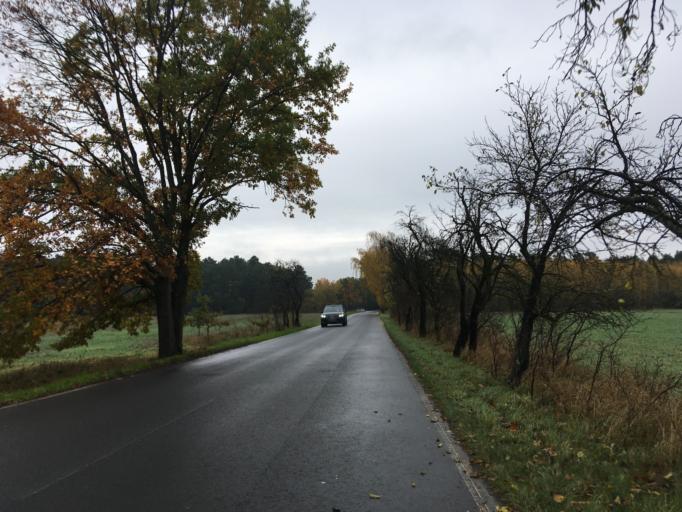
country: DE
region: Brandenburg
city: Friedland
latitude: 52.0460
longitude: 14.1849
